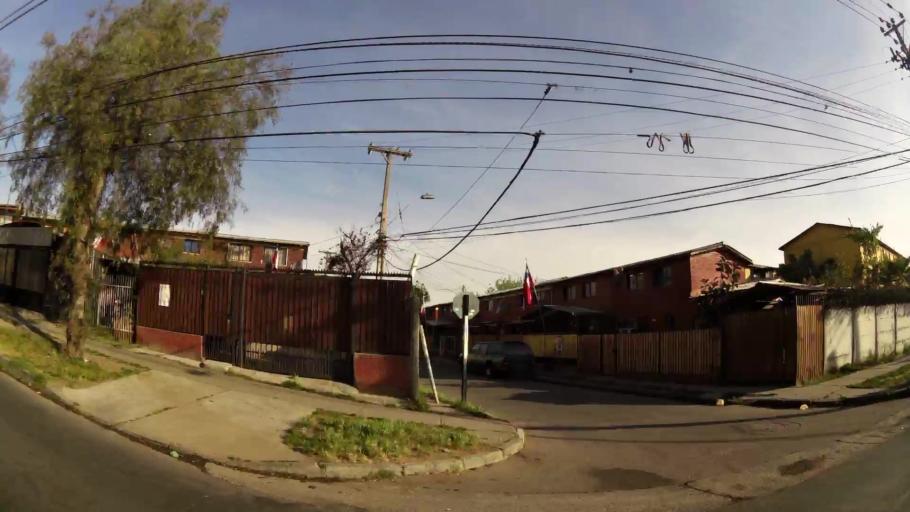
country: CL
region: Santiago Metropolitan
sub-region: Provincia de Cordillera
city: Puente Alto
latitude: -33.5529
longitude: -70.5724
